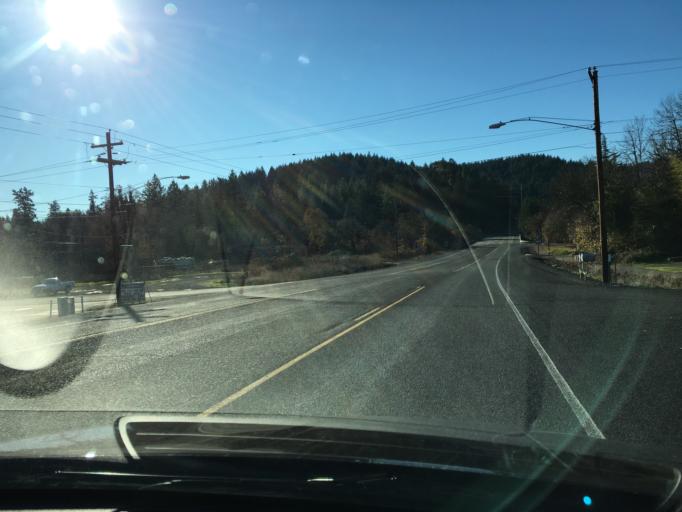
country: US
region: Oregon
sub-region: Douglas County
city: Glide
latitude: 43.2982
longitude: -123.0982
